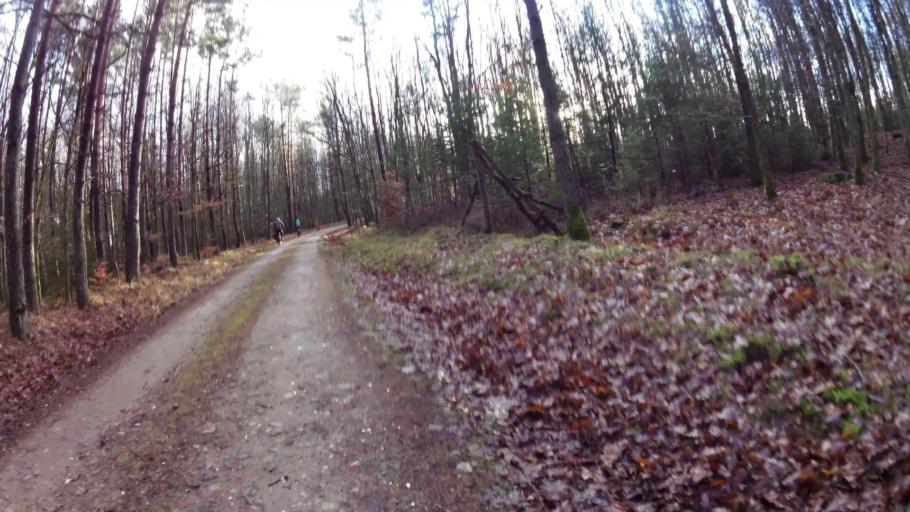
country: PL
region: West Pomeranian Voivodeship
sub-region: Powiat koszalinski
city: Sianow
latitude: 54.1126
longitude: 16.2987
